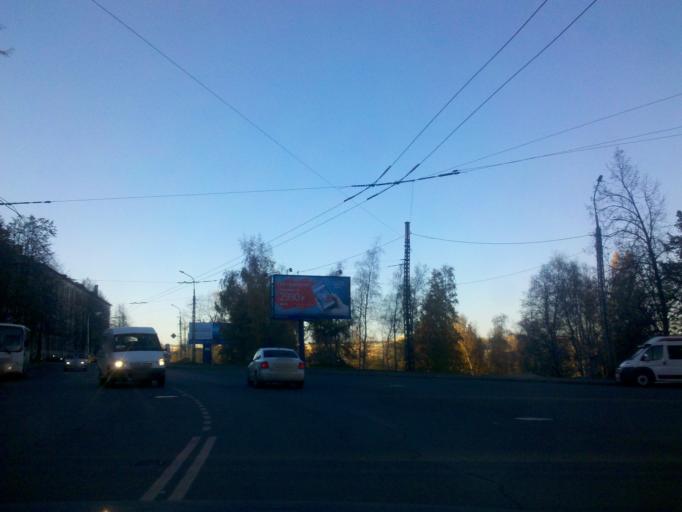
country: RU
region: Republic of Karelia
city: Petrozavodsk
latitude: 61.7827
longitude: 34.3854
